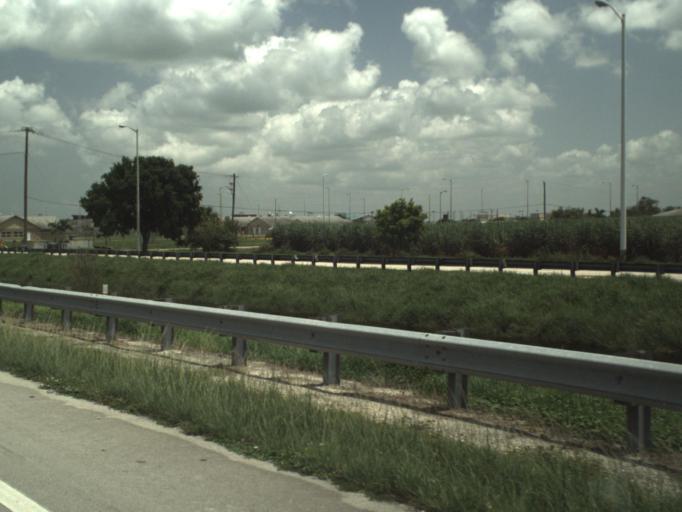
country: US
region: Florida
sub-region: Palm Beach County
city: Belle Glade
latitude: 26.7175
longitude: -80.6680
